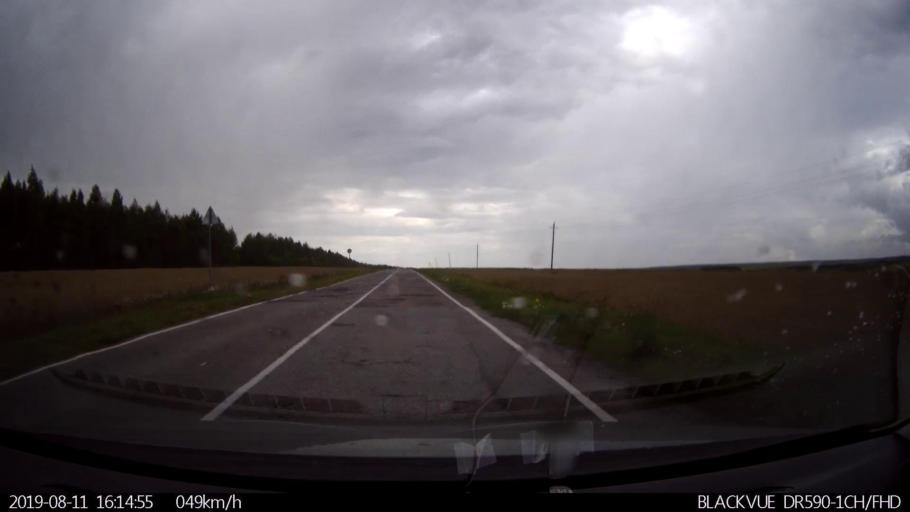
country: RU
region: Ulyanovsk
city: Mayna
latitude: 54.0314
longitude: 47.6312
